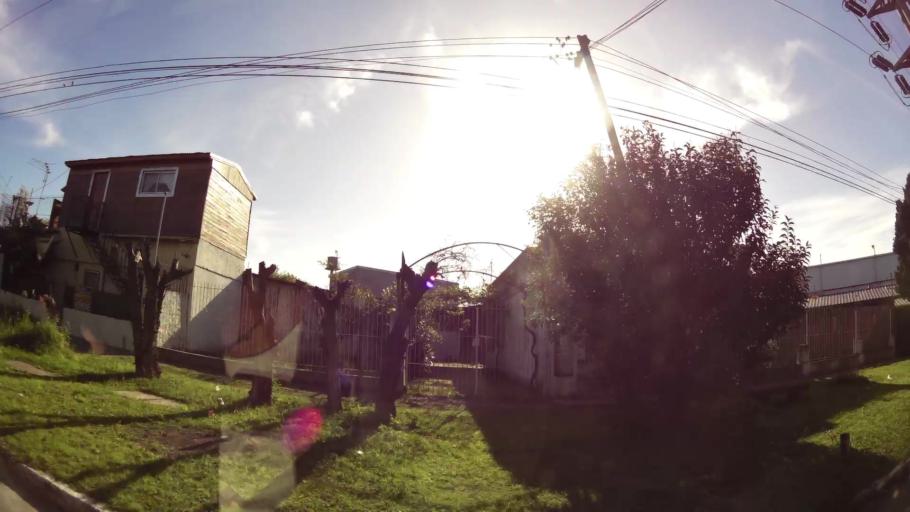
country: AR
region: Buenos Aires
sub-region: Partido de Quilmes
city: Quilmes
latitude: -34.8024
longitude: -58.2169
